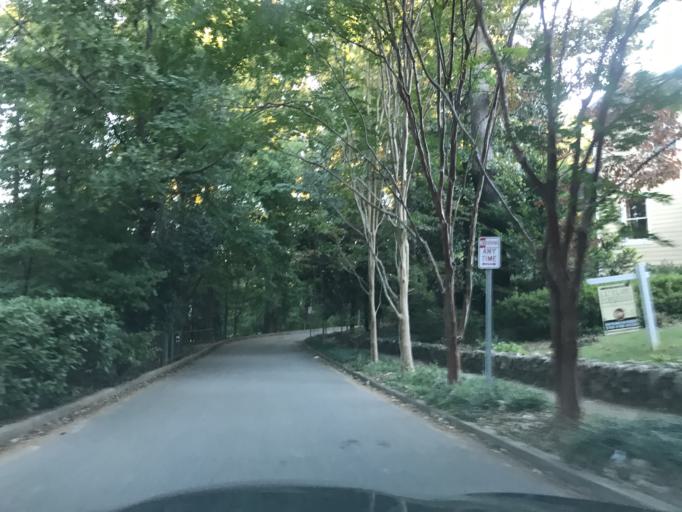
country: US
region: North Carolina
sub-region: Wake County
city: West Raleigh
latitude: 35.7881
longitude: -78.6564
